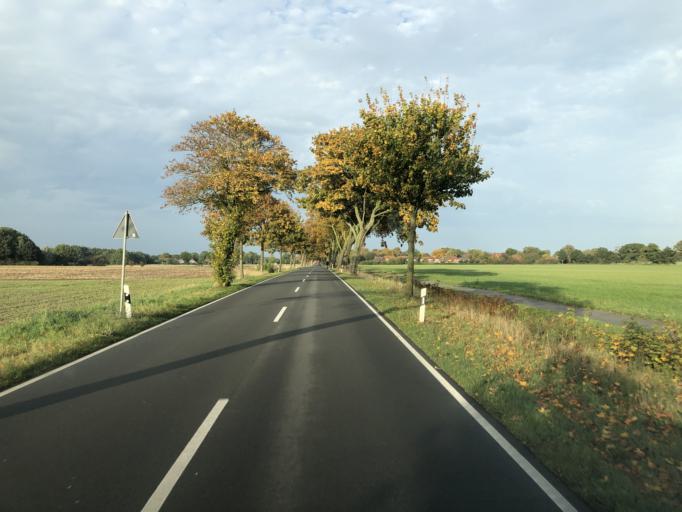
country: DE
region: Lower Saxony
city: Neu Wulmstorf
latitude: 53.4316
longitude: 9.7980
